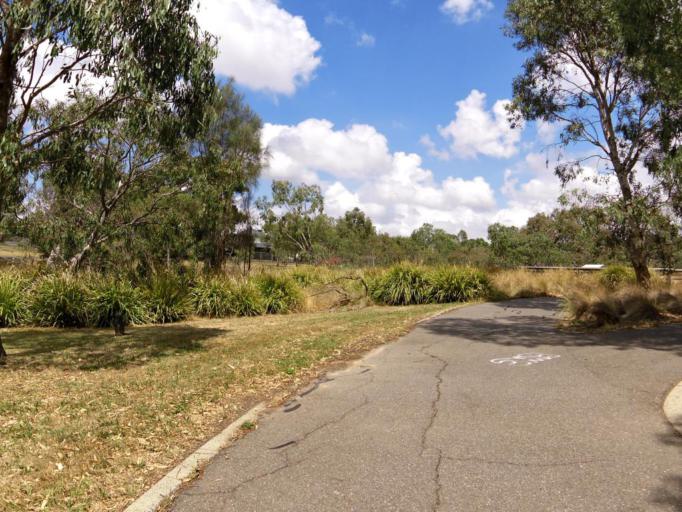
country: AU
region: Victoria
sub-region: Hume
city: Craigieburn
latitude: -37.5858
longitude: 144.9338
